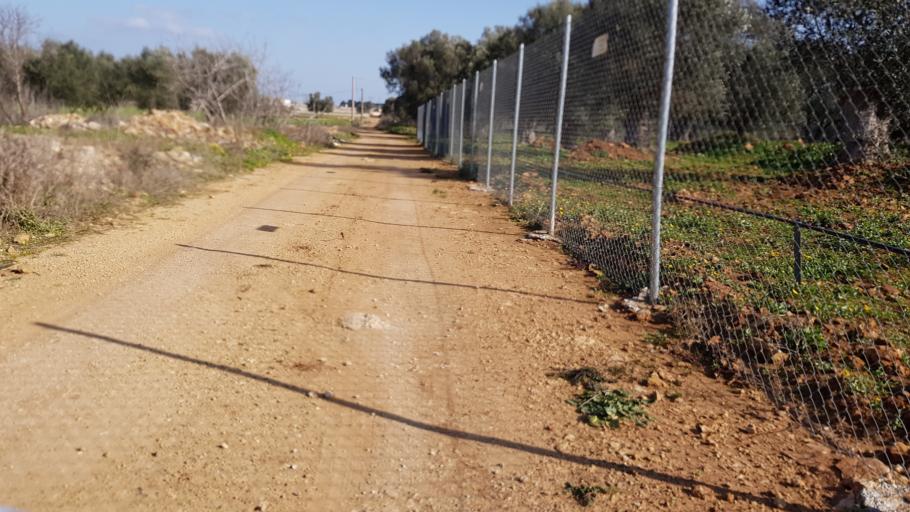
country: IT
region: Apulia
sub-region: Provincia di Brindisi
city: Mesagne
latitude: 40.5914
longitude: 17.8699
